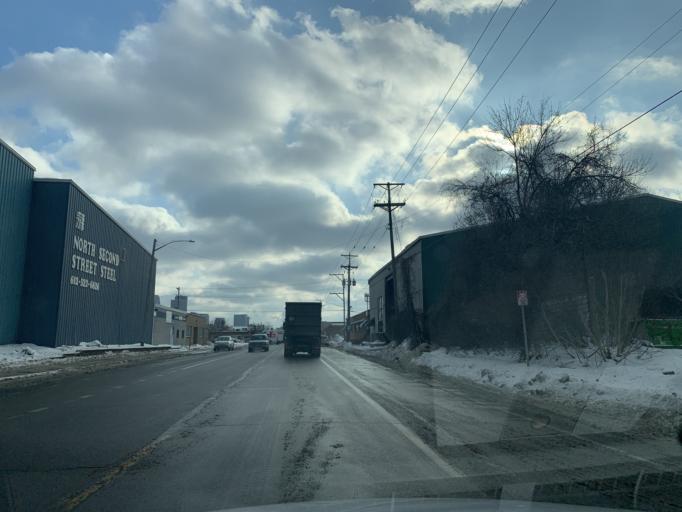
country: US
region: Minnesota
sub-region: Hennepin County
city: Minneapolis
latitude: 45.0026
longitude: -93.2802
